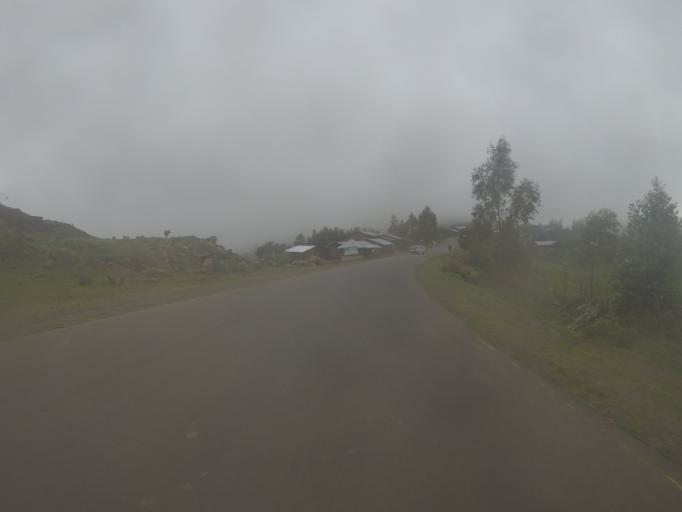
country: ET
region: Amhara
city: Gondar
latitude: 12.7426
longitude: 37.5157
